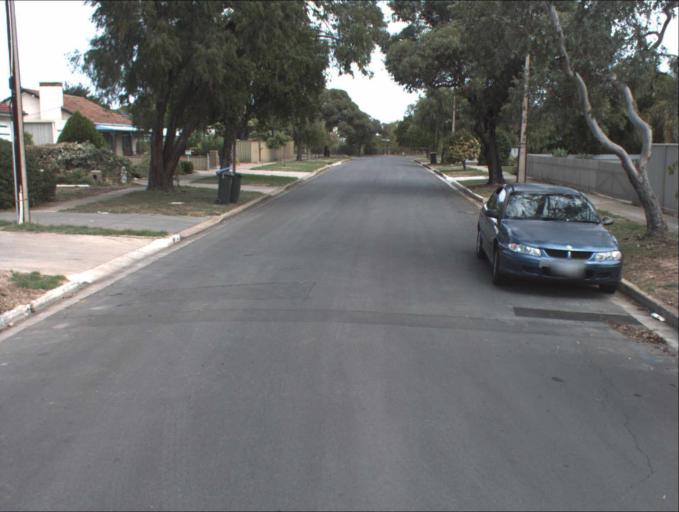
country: AU
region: South Australia
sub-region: Port Adelaide Enfield
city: Enfield
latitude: -34.8547
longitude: 138.6131
